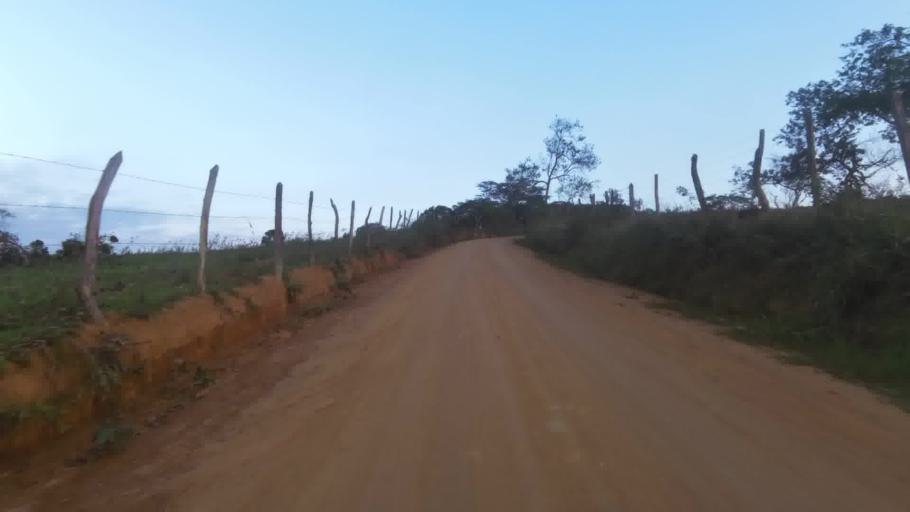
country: BR
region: Espirito Santo
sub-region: Guarapari
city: Guarapari
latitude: -20.6967
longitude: -40.5738
